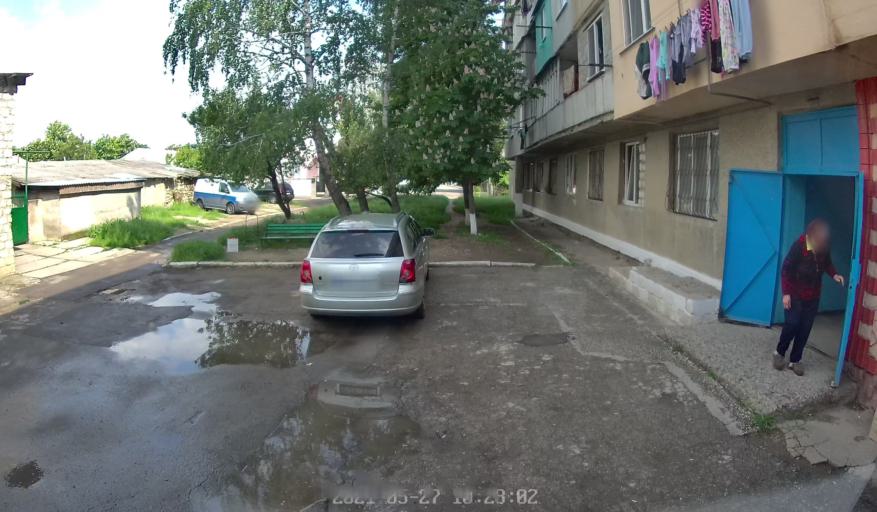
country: MD
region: Chisinau
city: Stauceni
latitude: 47.0889
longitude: 28.8693
